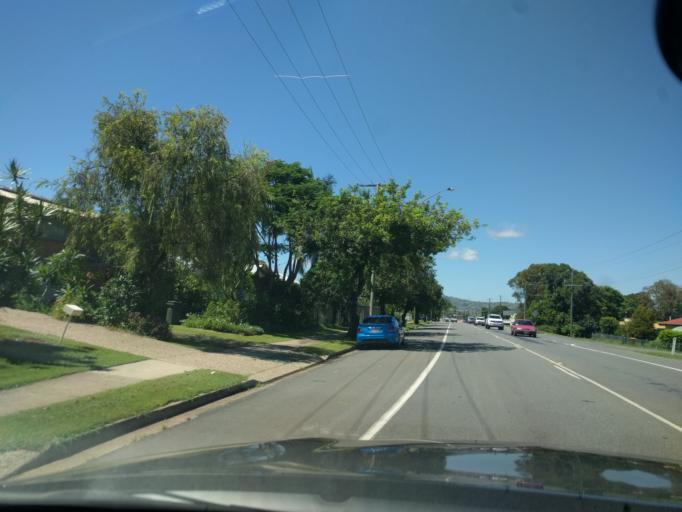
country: AU
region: Queensland
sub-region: Logan
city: Cedar Vale
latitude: -27.9736
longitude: 152.9950
